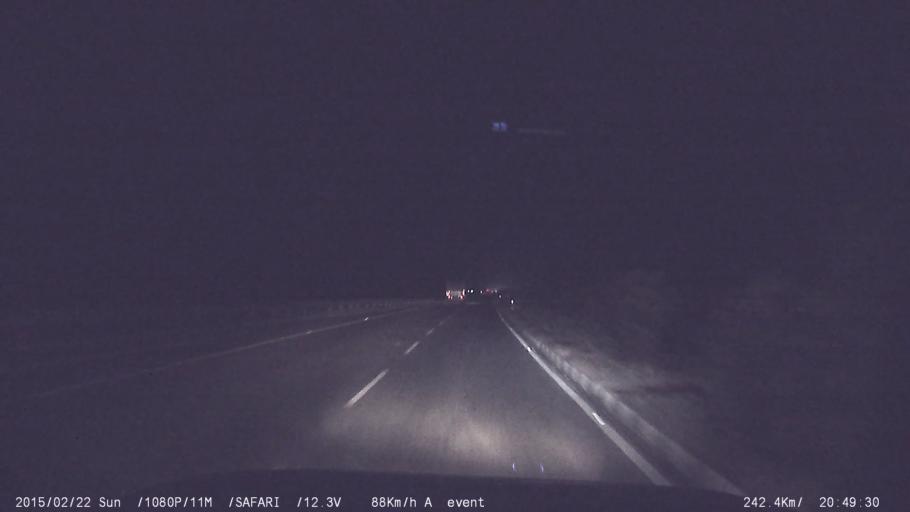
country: IN
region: Tamil Nadu
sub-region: Dindigul
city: Vedasandur
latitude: 10.5187
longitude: 77.9350
